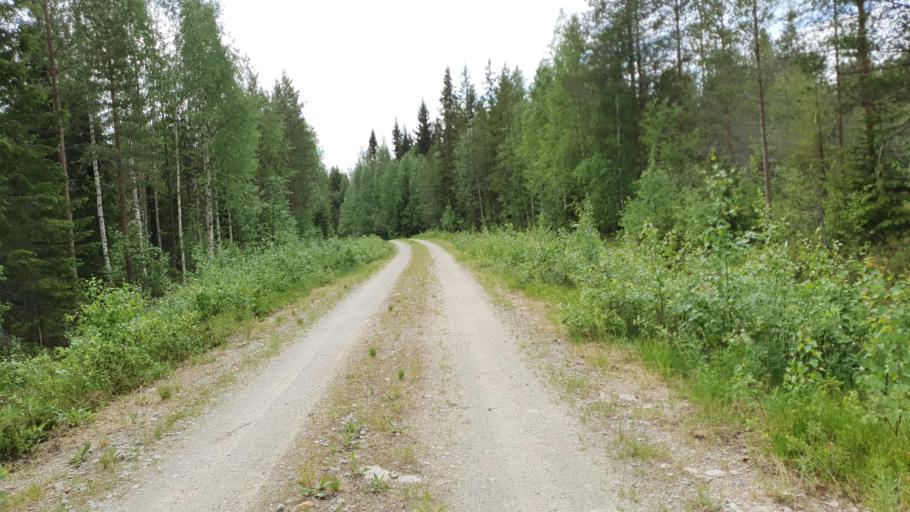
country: FI
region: Kainuu
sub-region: Kehys-Kainuu
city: Kuhmo
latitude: 64.4557
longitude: 29.6597
